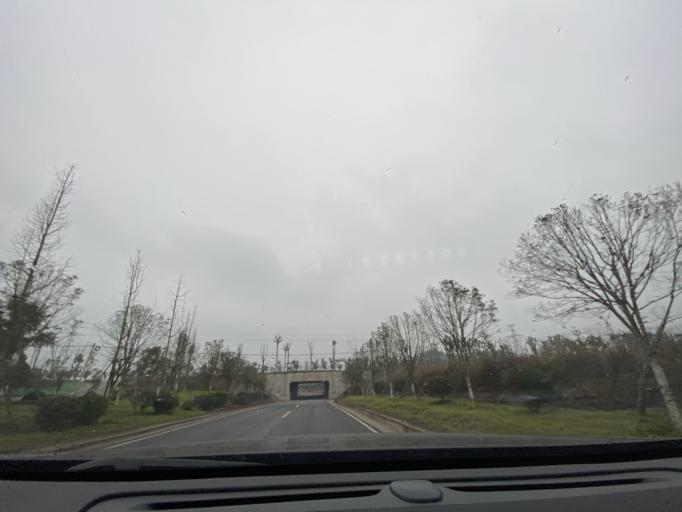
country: CN
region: Sichuan
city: Jiancheng
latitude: 30.3939
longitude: 104.6342
